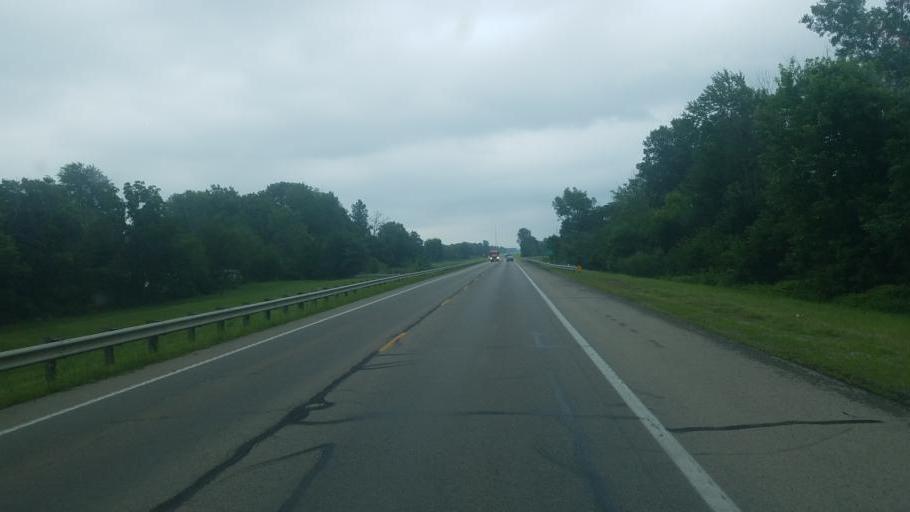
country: US
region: Ohio
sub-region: Logan County
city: Russells Point
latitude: 40.4656
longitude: -83.8805
